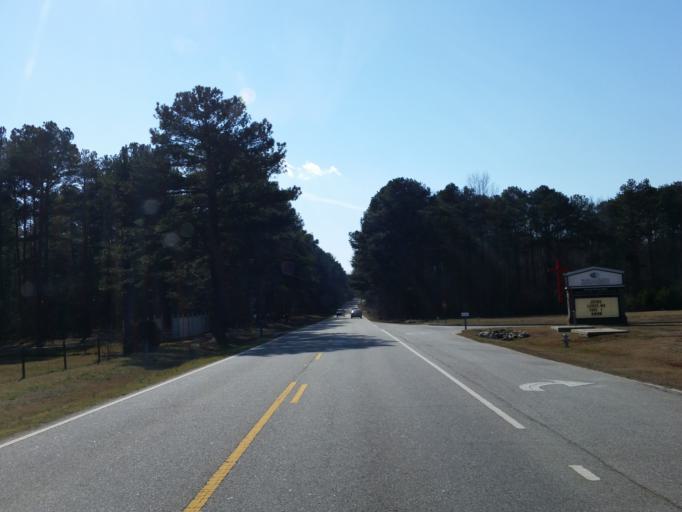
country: US
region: Georgia
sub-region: Henry County
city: Hampton
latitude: 33.4434
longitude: -84.2399
